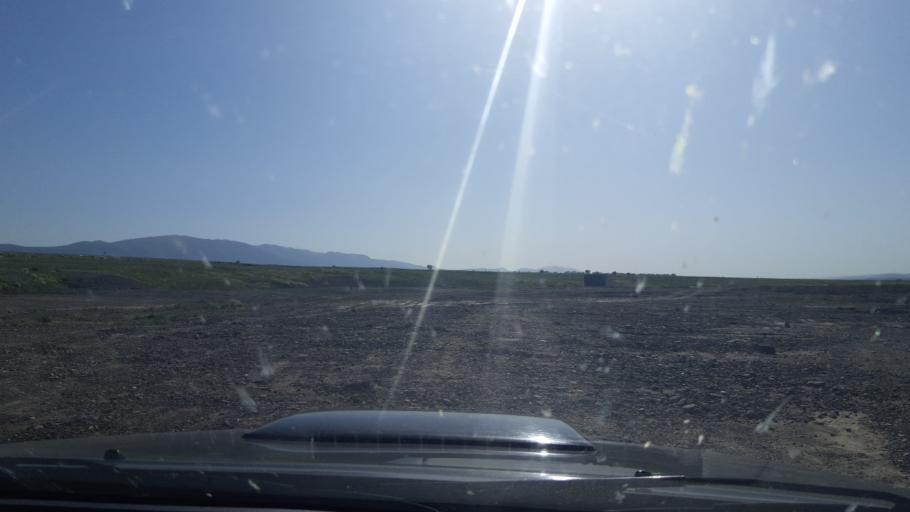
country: KZ
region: Ongtustik Qazaqstan
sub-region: Tulkibas Audany
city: Zhabagly
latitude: 42.5090
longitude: 70.4635
